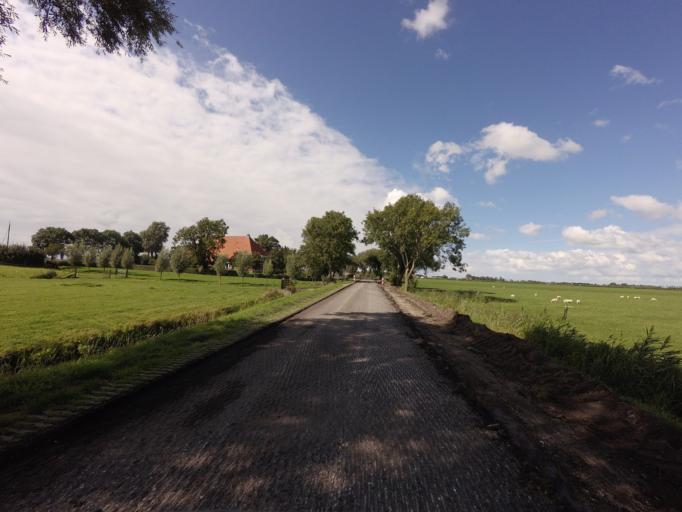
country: NL
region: Friesland
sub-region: Sudwest Fryslan
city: Bolsward
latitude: 53.0348
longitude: 5.5651
